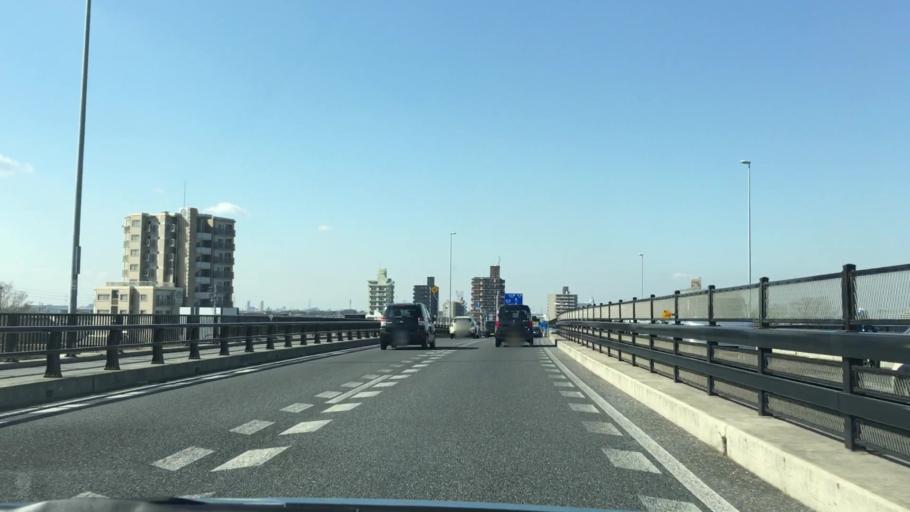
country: JP
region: Aichi
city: Okazaki
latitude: 34.9593
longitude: 137.1489
